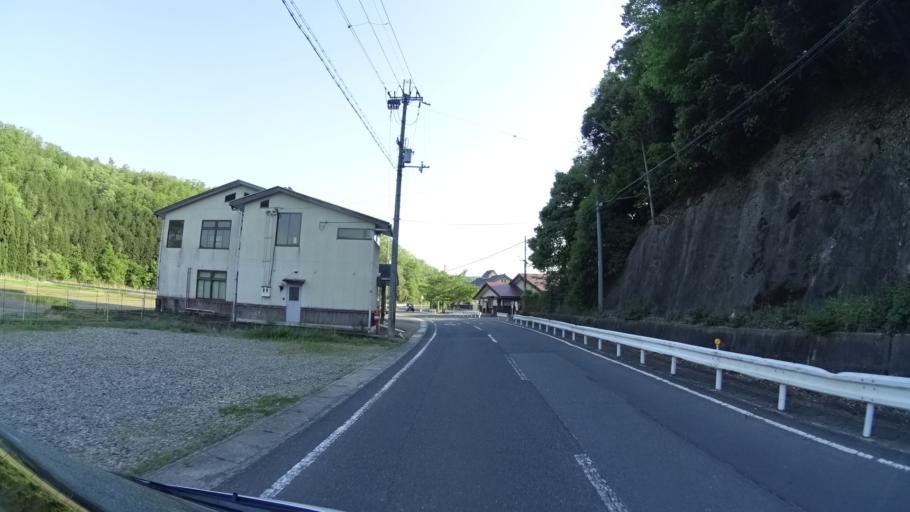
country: JP
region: Hyogo
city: Sasayama
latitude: 35.1362
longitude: 135.4156
